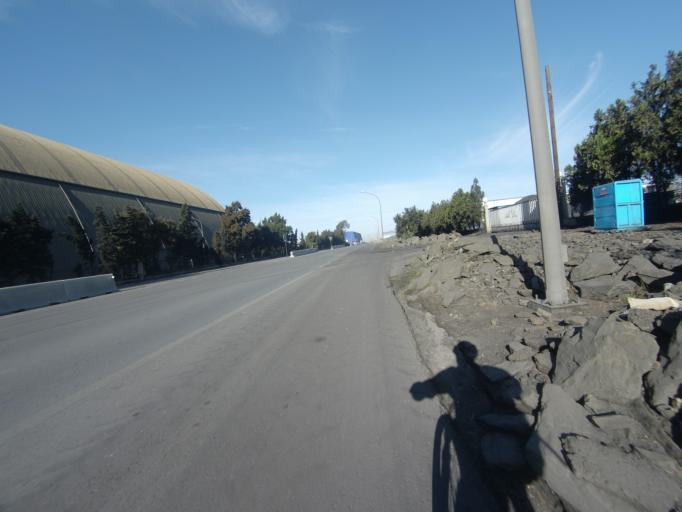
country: ES
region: Andalusia
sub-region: Provincia de Huelva
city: Punta Umbria
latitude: 37.1854
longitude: -6.9258
